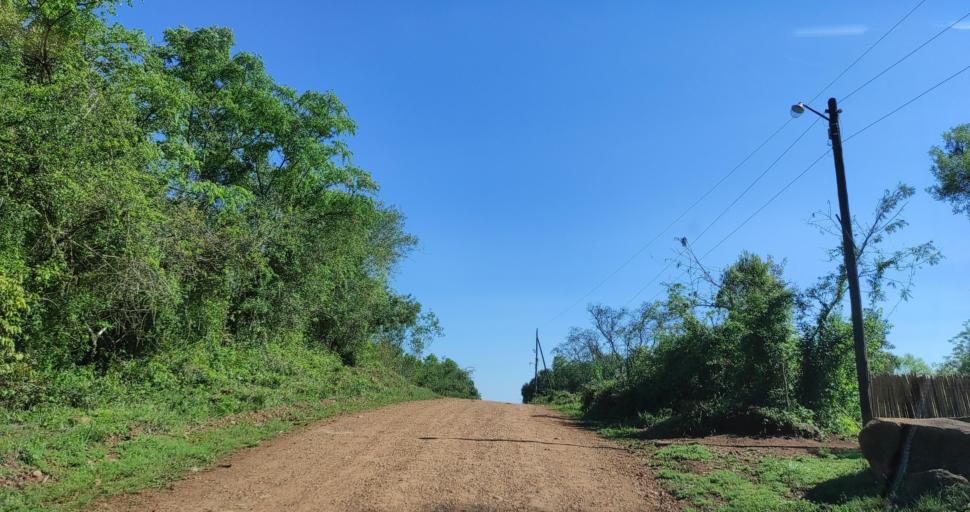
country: AR
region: Misiones
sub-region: Departamento de Candelaria
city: Loreto
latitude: -27.3163
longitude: -55.5346
